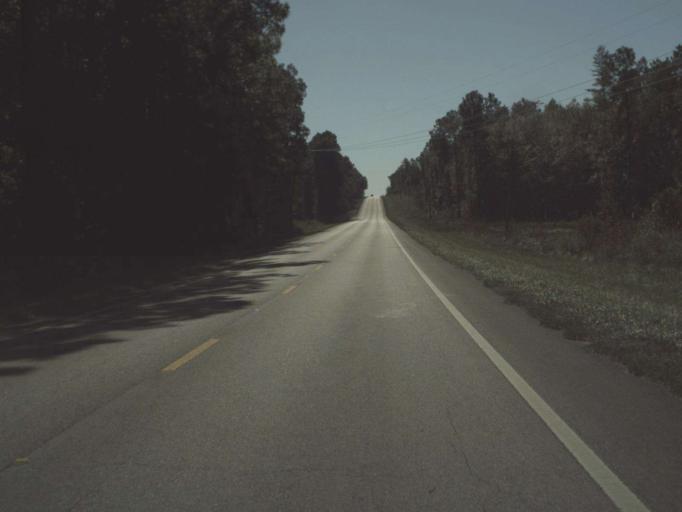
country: US
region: Florida
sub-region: Walton County
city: DeFuniak Springs
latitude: 30.9046
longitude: -86.1314
